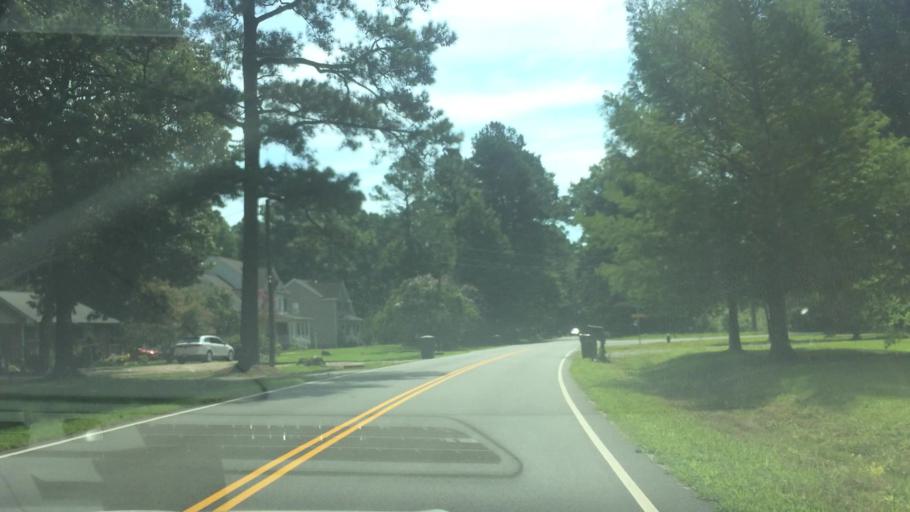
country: US
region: Virginia
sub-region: City of Poquoson
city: Poquoson
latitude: 37.1688
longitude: -76.4354
